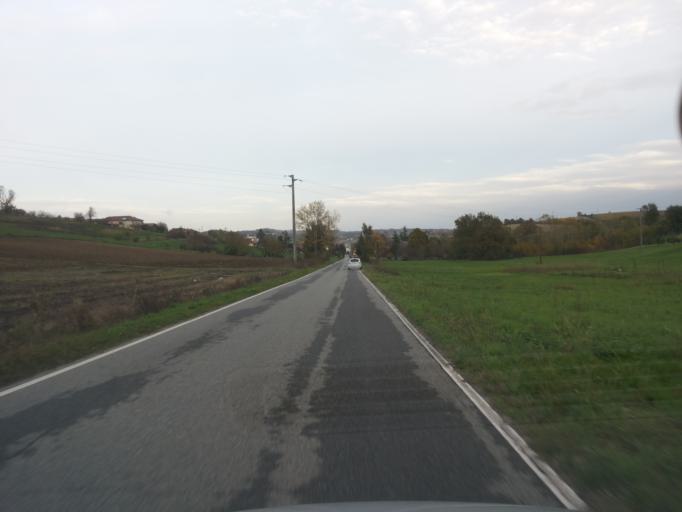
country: IT
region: Piedmont
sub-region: Provincia di Alessandria
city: Serralunga di Crea
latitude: 45.0999
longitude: 8.2969
